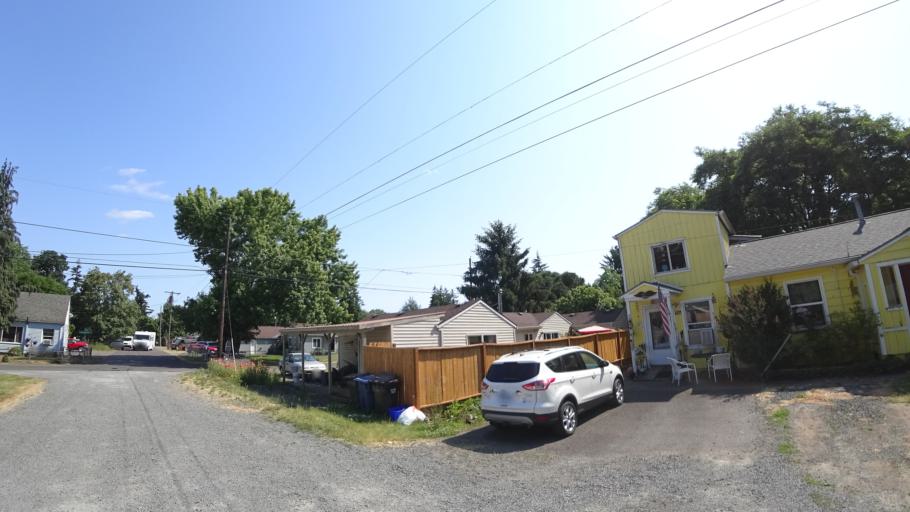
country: US
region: Oregon
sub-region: Clackamas County
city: Oatfield
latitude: 45.4508
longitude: -122.5952
